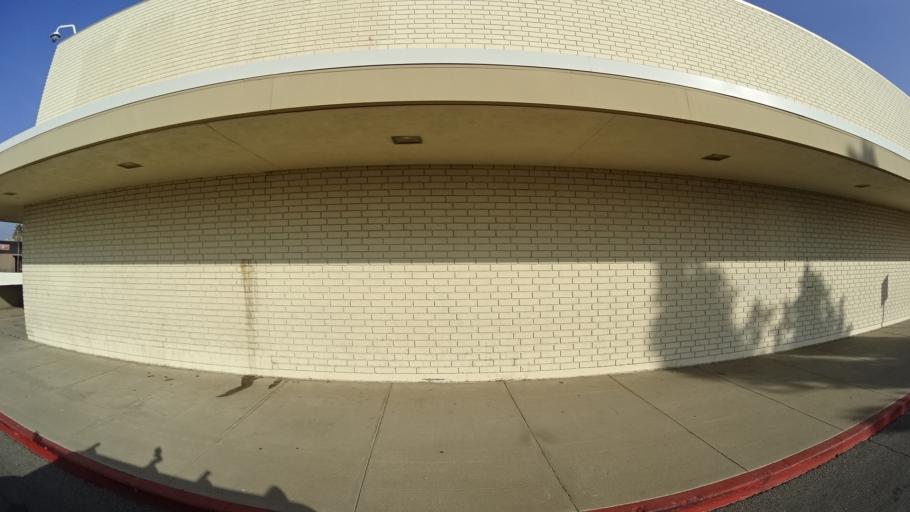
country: US
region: California
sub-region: Kern County
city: Bakersfield
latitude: 35.3380
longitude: -119.0362
